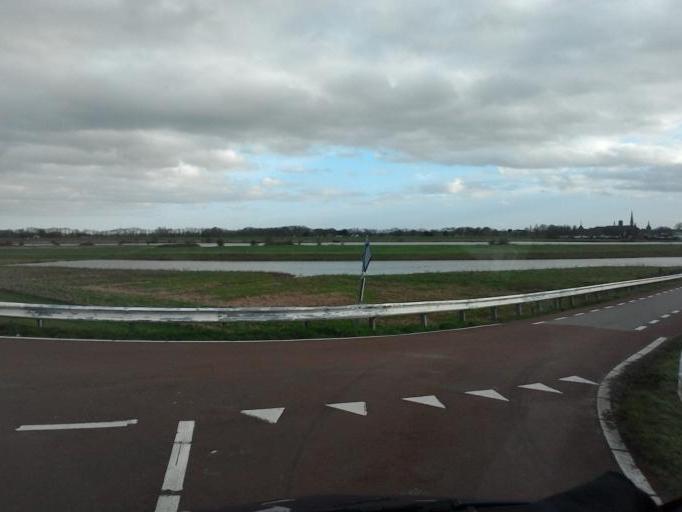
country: NL
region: Gelderland
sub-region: Gemeente Culemborg
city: Culemborg
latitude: 51.9678
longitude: 5.2152
